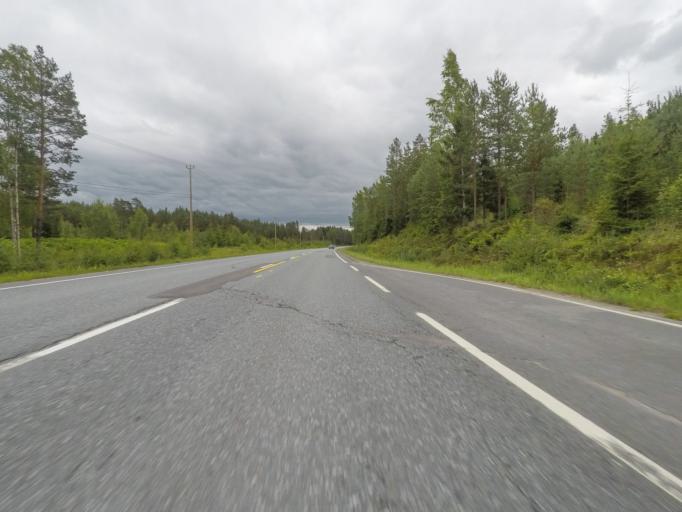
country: FI
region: Varsinais-Suomi
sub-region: Salo
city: Muurla
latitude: 60.3152
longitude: 23.3078
